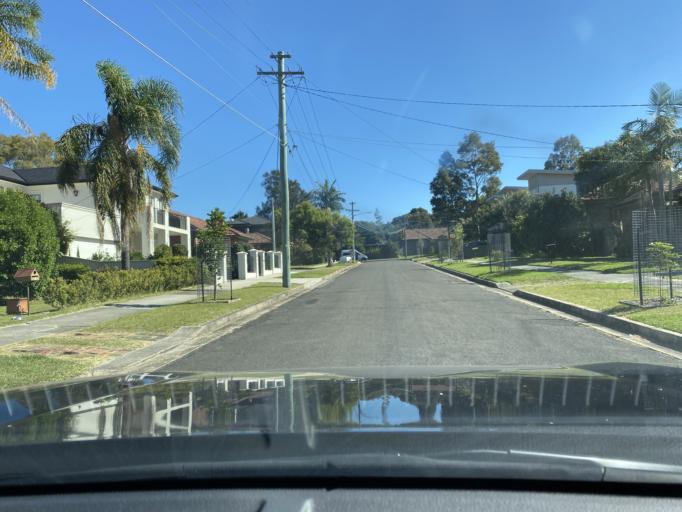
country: AU
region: New South Wales
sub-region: Canada Bay
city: Wareemba
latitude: -33.8533
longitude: 151.1335
